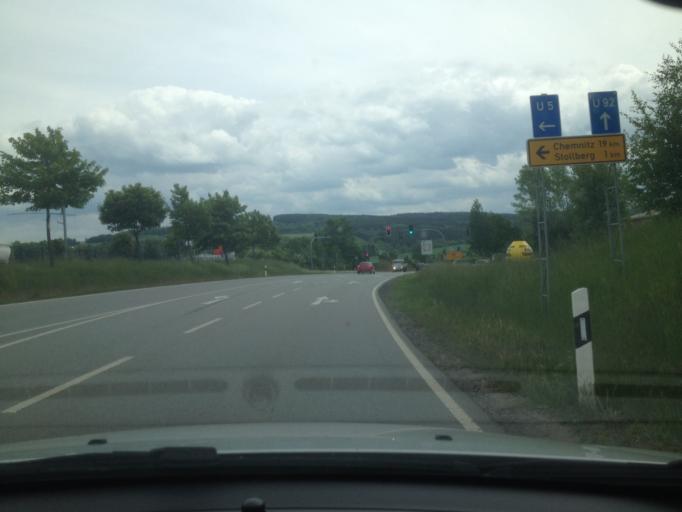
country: DE
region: Saxony
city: Stollberg
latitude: 50.7001
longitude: 12.7660
